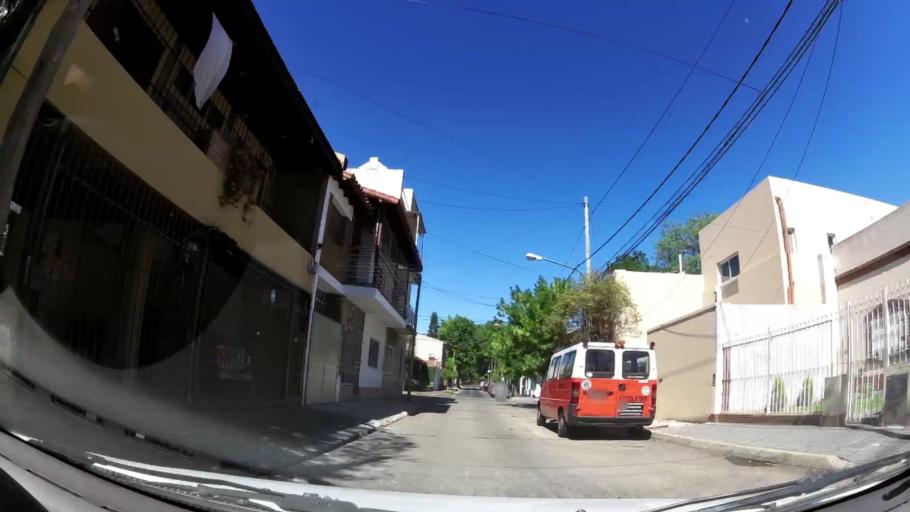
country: AR
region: Buenos Aires
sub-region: Partido de Vicente Lopez
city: Olivos
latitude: -34.5235
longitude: -58.4954
